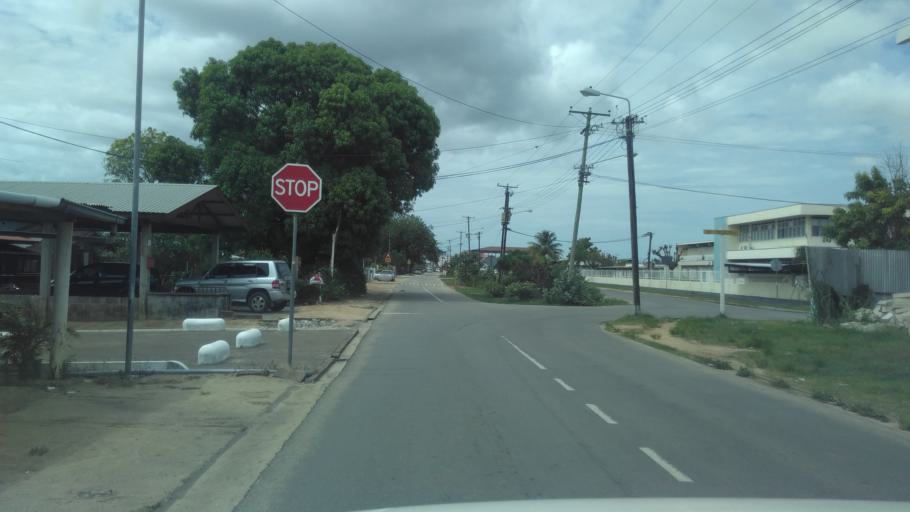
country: SR
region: Paramaribo
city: Paramaribo
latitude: 5.8511
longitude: -55.1308
